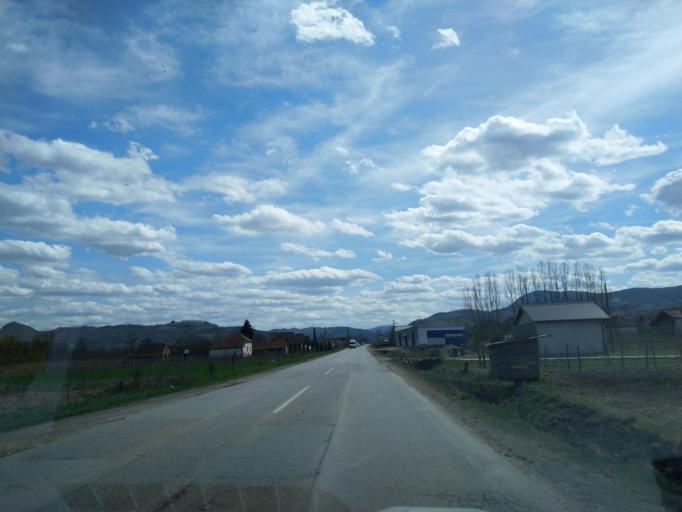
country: RS
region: Central Serbia
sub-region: Zlatiborski Okrug
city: Arilje
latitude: 43.7287
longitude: 20.1118
